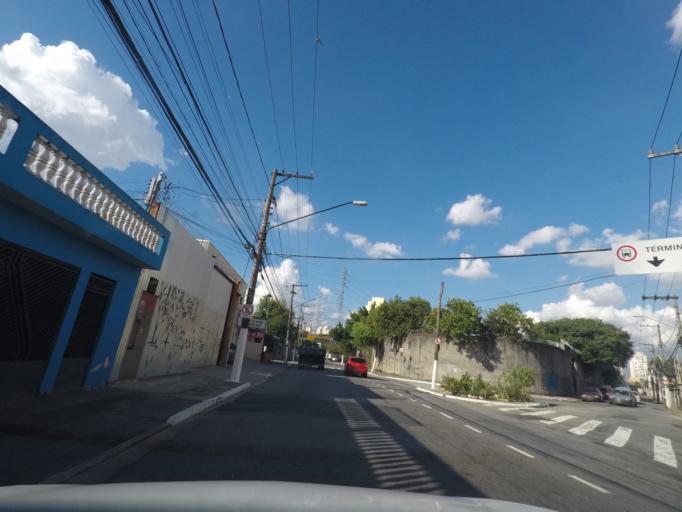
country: BR
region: Sao Paulo
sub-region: Sao Paulo
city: Sao Paulo
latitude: -23.5045
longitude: -46.6864
